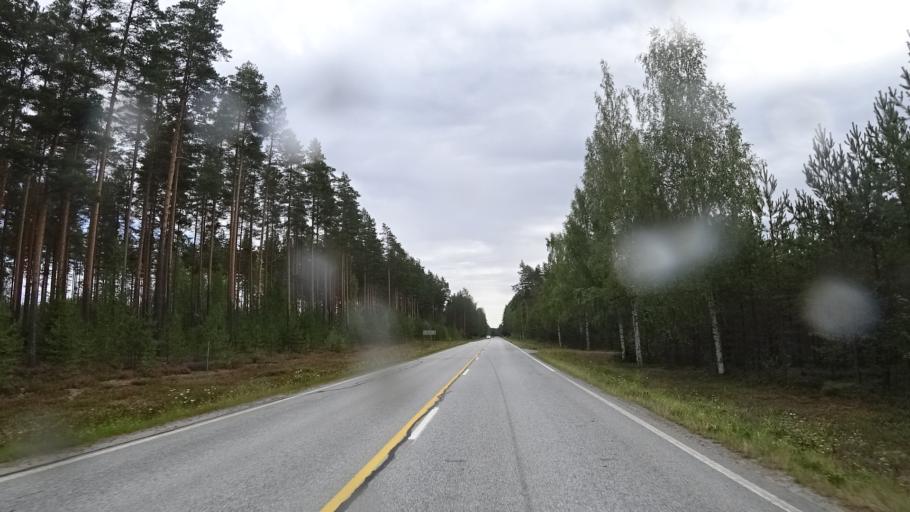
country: FI
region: North Karelia
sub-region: Keski-Karjala
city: Raeaekkylae
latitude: 62.1106
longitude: 29.7280
